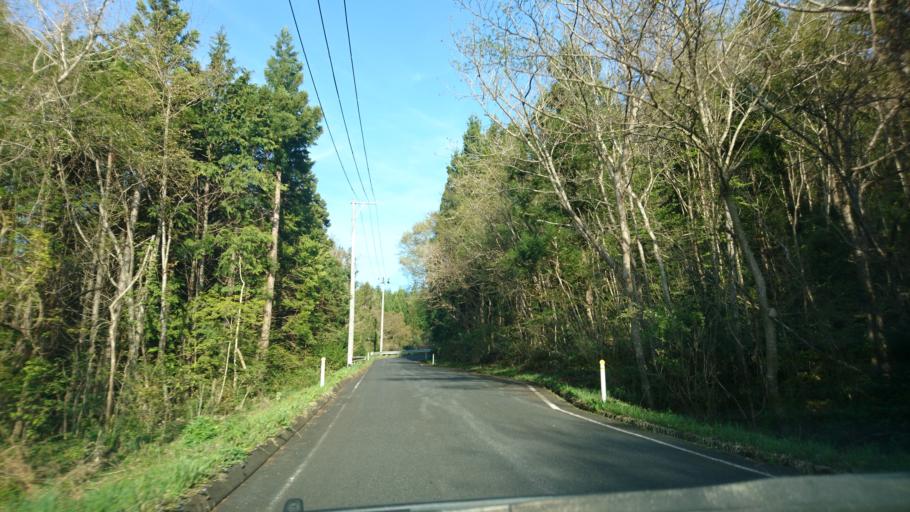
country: JP
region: Iwate
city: Ichinoseki
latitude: 38.8902
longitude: 141.2910
